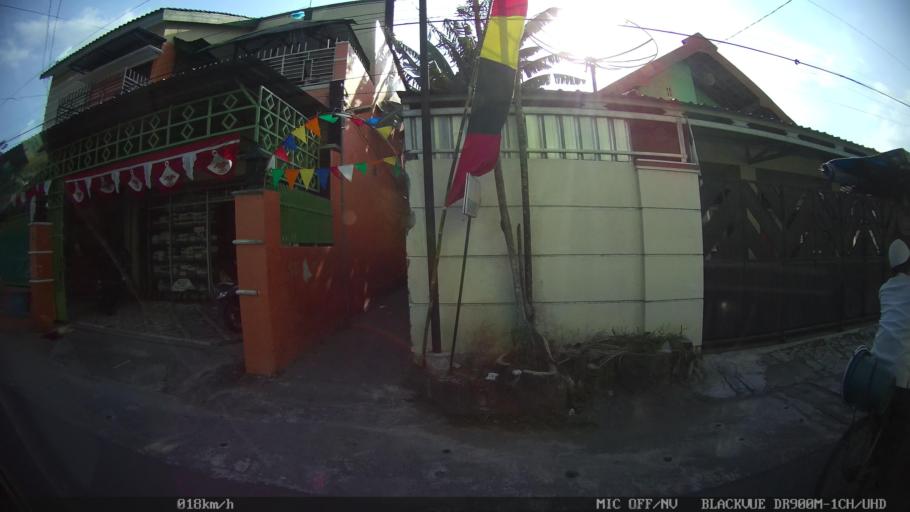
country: ID
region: Daerah Istimewa Yogyakarta
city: Yogyakarta
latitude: -7.8195
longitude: 110.3794
